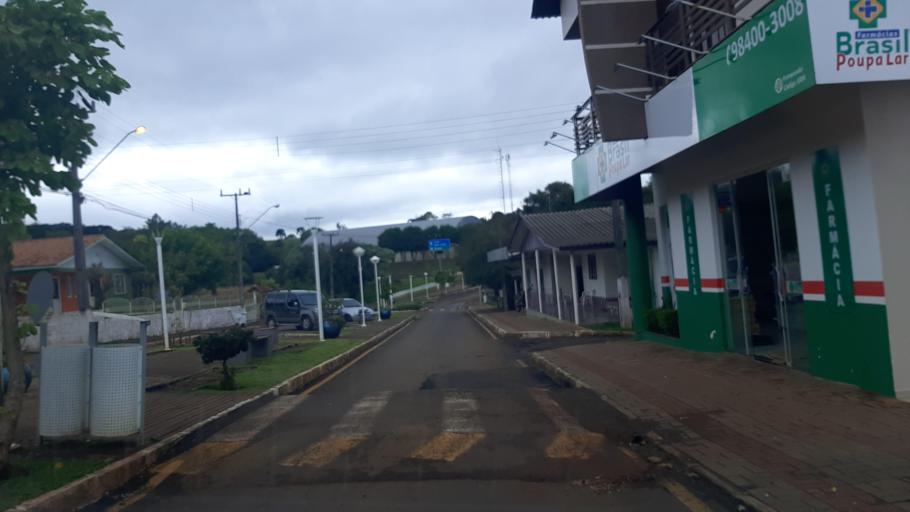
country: BR
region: Parana
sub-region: Ampere
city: Ampere
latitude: -26.0343
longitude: -53.4855
